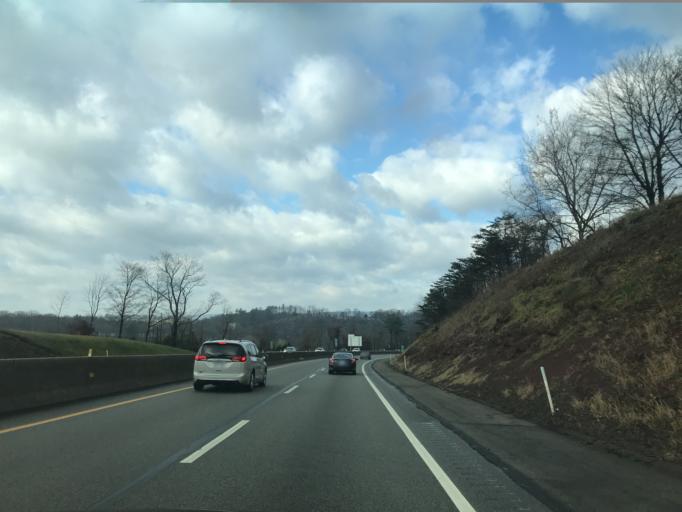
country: US
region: Pennsylvania
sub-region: Bedford County
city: Earlston
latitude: 39.9861
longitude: -78.2995
